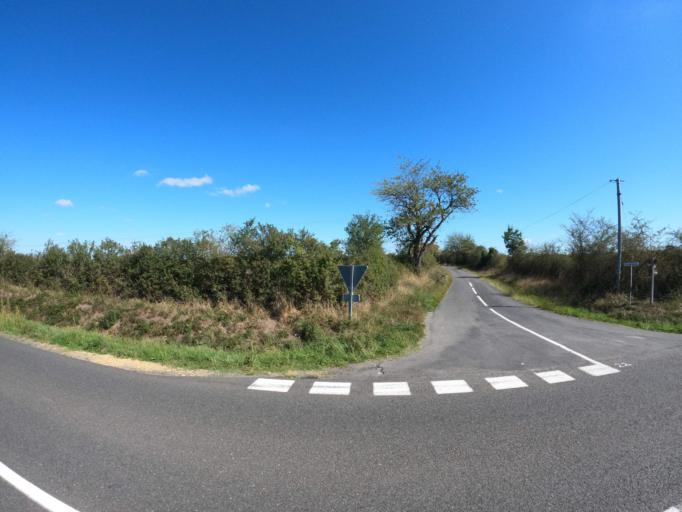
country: FR
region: Poitou-Charentes
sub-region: Departement de la Vienne
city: Saulge
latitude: 46.3822
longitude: 0.9188
